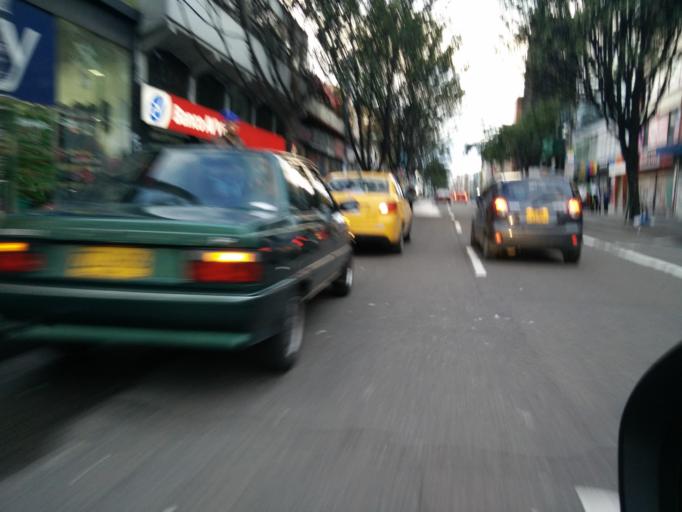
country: CO
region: Bogota D.C.
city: Bogota
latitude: 4.6486
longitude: -74.0637
